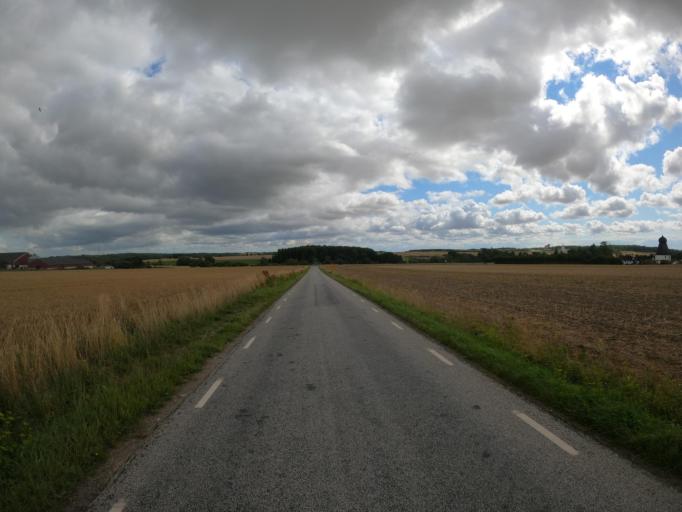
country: SE
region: Skane
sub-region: Lunds Kommun
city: Lund
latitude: 55.7171
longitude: 13.3014
